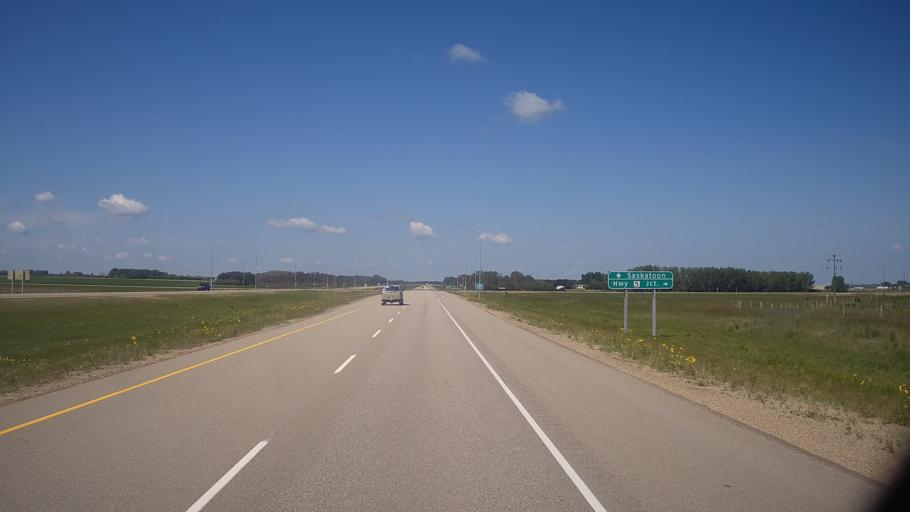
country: CA
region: Saskatchewan
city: Saskatoon
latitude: 52.0123
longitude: -106.3804
